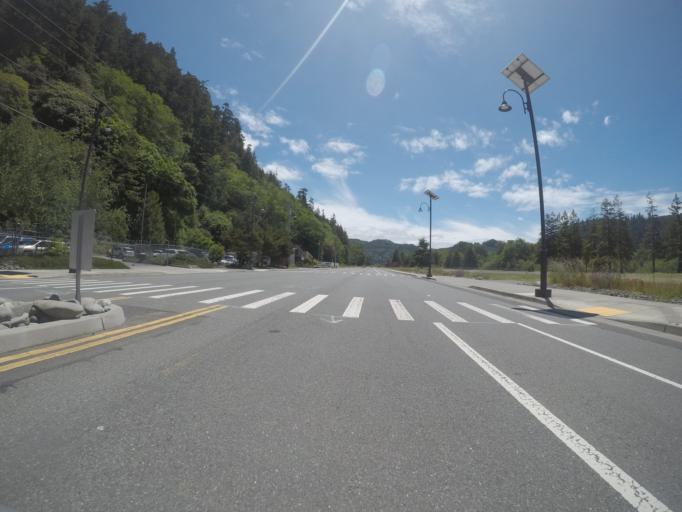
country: US
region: California
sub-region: Del Norte County
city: Bertsch-Oceanview
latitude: 41.5289
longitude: -124.0379
